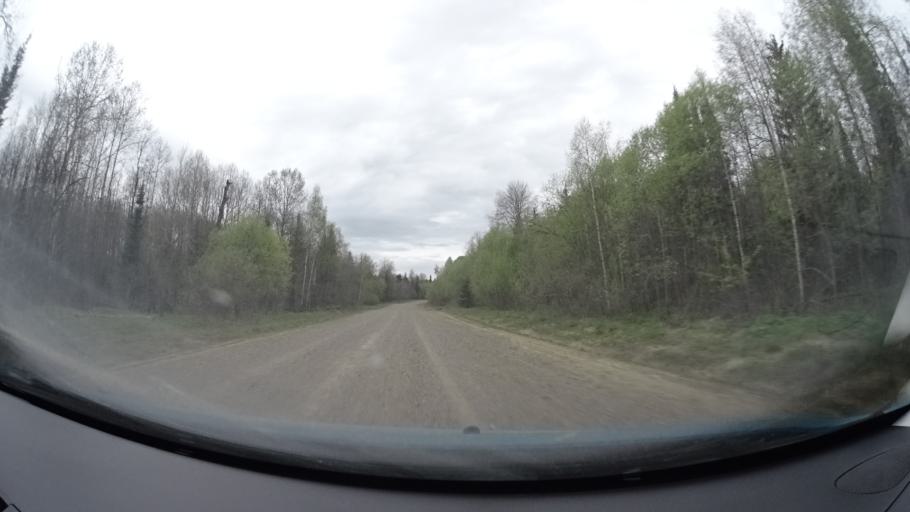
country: RU
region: Perm
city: Kuyeda
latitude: 56.5930
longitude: 55.7051
